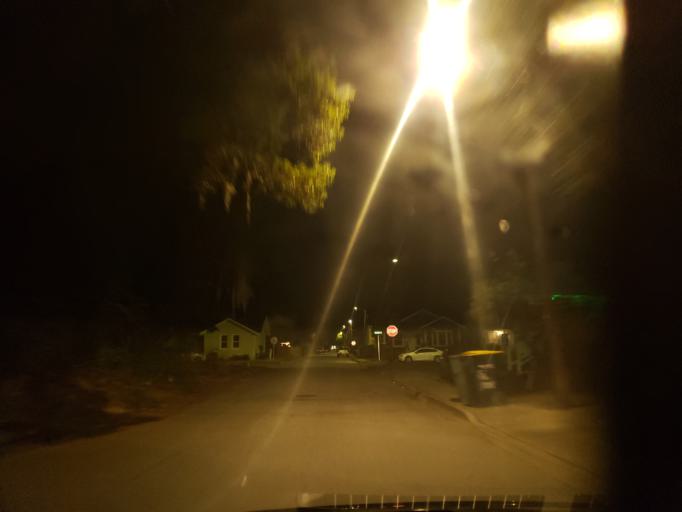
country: US
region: Georgia
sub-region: Chatham County
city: Thunderbolt
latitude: 32.0519
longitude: -81.0600
